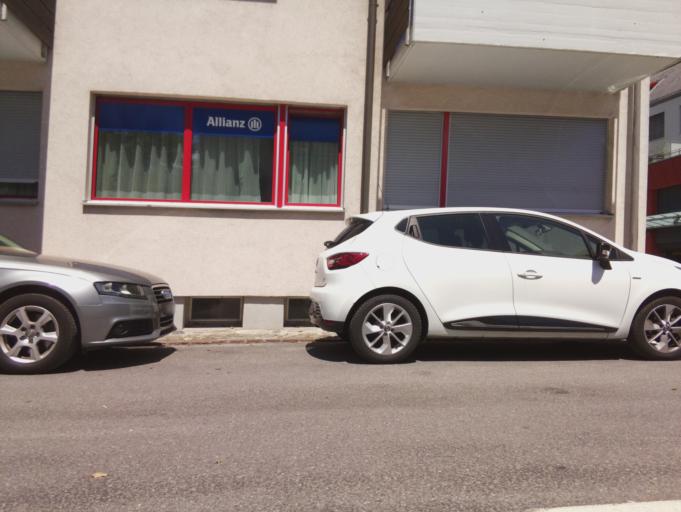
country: CH
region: Glarus
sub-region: Glarus
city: Glarus
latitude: 47.0413
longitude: 9.0701
